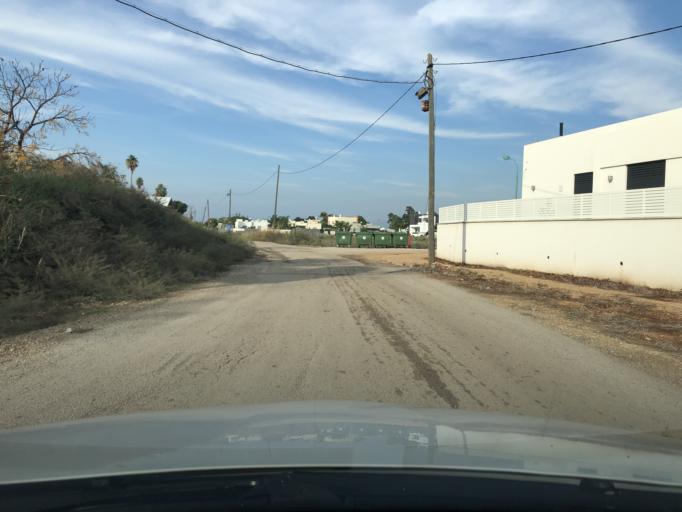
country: IL
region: Northern District
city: Yavne'el
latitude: 32.6594
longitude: 35.5855
